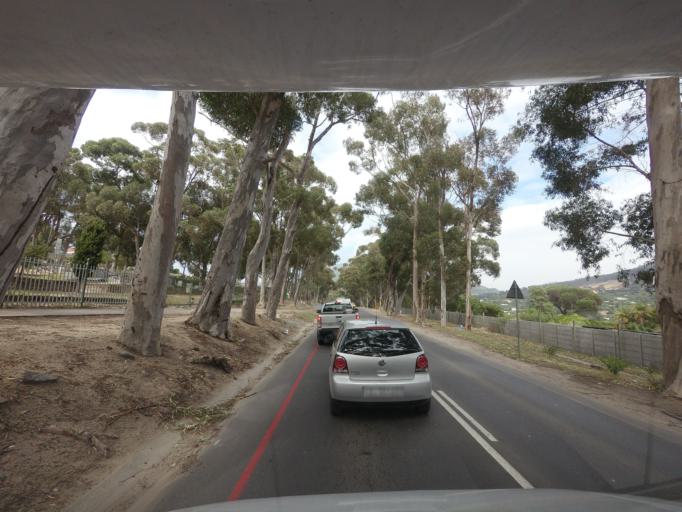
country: ZA
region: Western Cape
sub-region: City of Cape Town
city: Constantia
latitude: -34.0235
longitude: 18.3631
